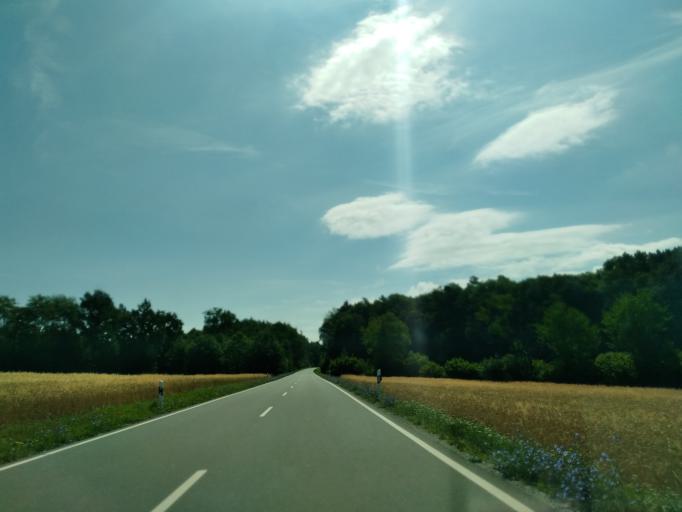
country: DE
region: Baden-Wuerttemberg
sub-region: Karlsruhe Region
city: Mudau
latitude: 49.5107
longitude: 9.2219
